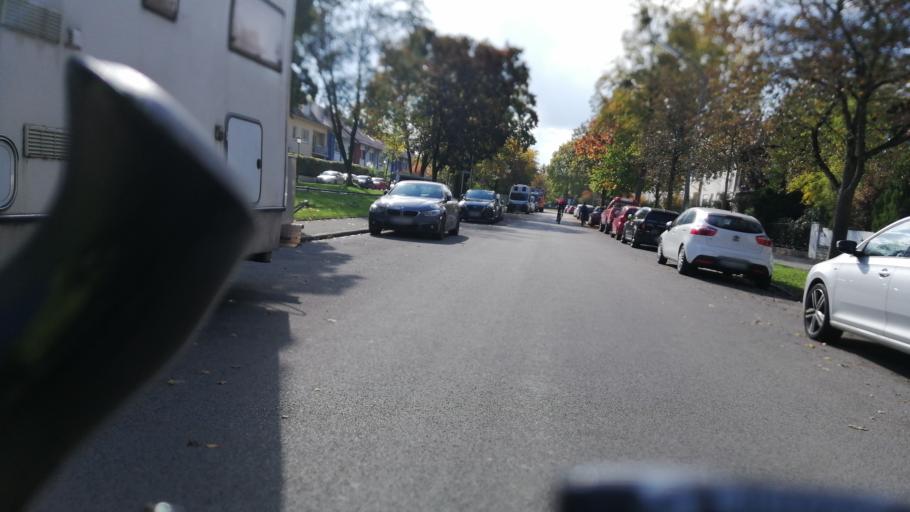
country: DE
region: Bavaria
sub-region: Upper Bavaria
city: Pasing
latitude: 48.1338
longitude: 11.4947
